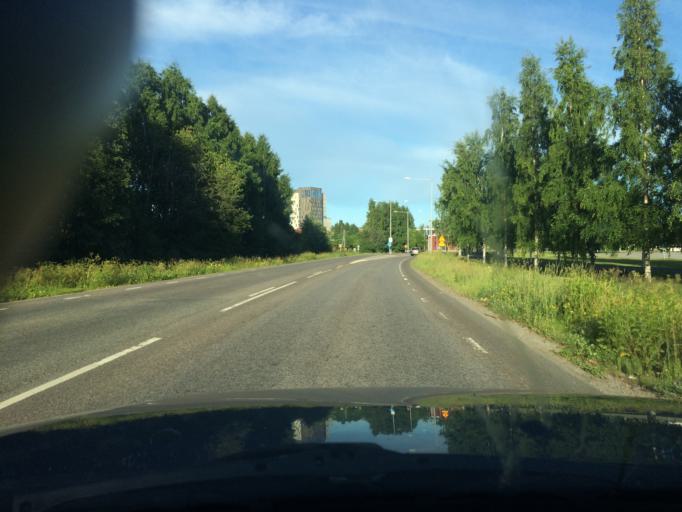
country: SE
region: Norrbotten
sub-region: Pitea Kommun
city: Pitea
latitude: 65.3174
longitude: 21.4660
